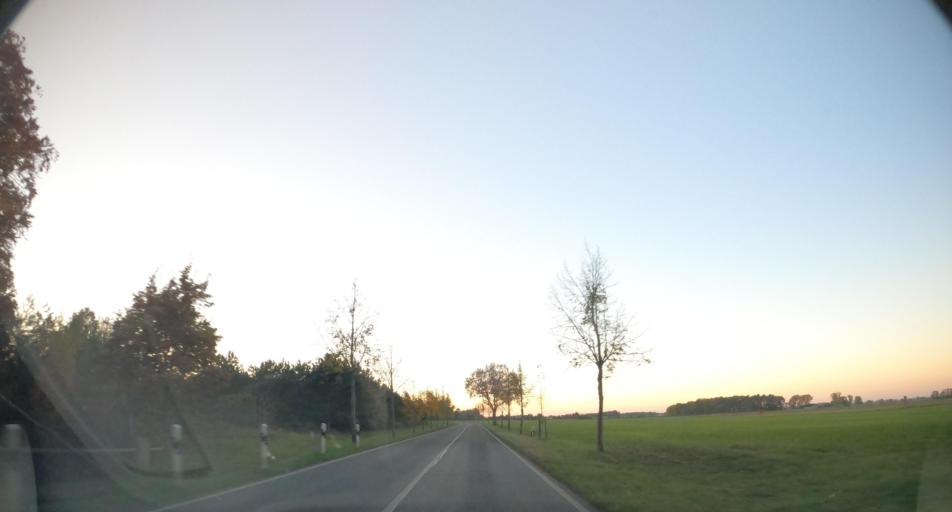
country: DE
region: Mecklenburg-Vorpommern
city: Usedom
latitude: 53.7687
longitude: 13.9200
